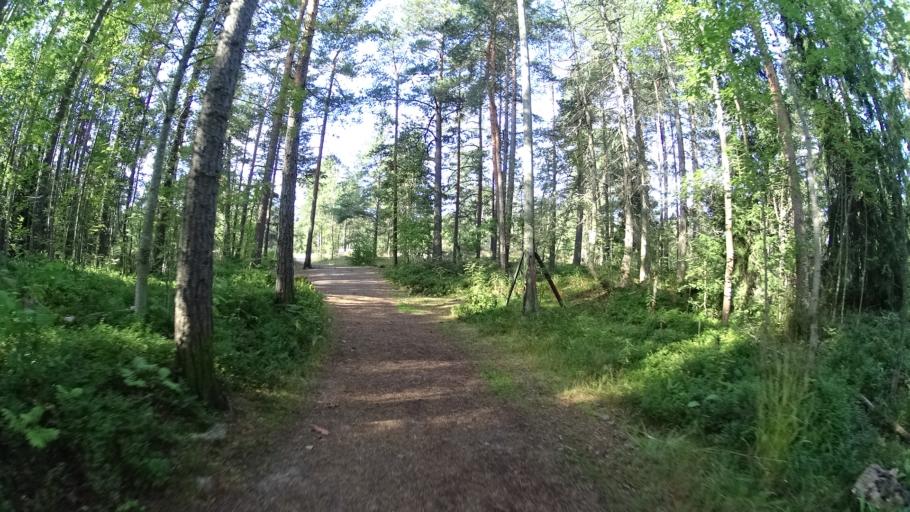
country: FI
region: Uusimaa
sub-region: Helsinki
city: Kilo
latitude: 60.2314
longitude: 24.7606
